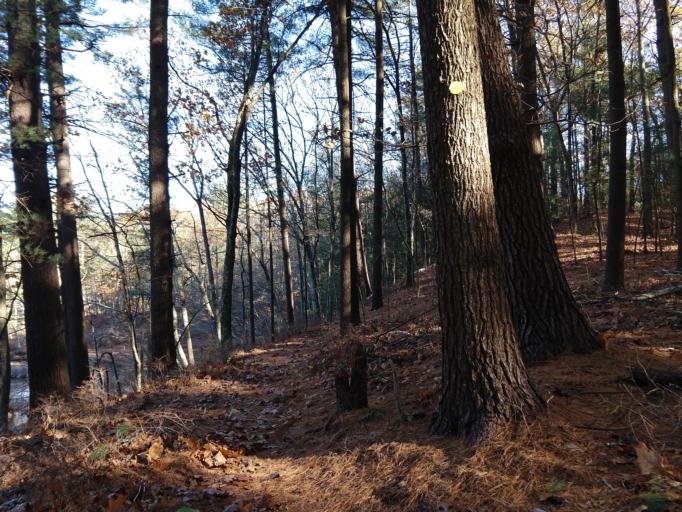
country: US
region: Massachusetts
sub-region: Middlesex County
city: Concord
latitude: 42.4871
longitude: -71.3235
